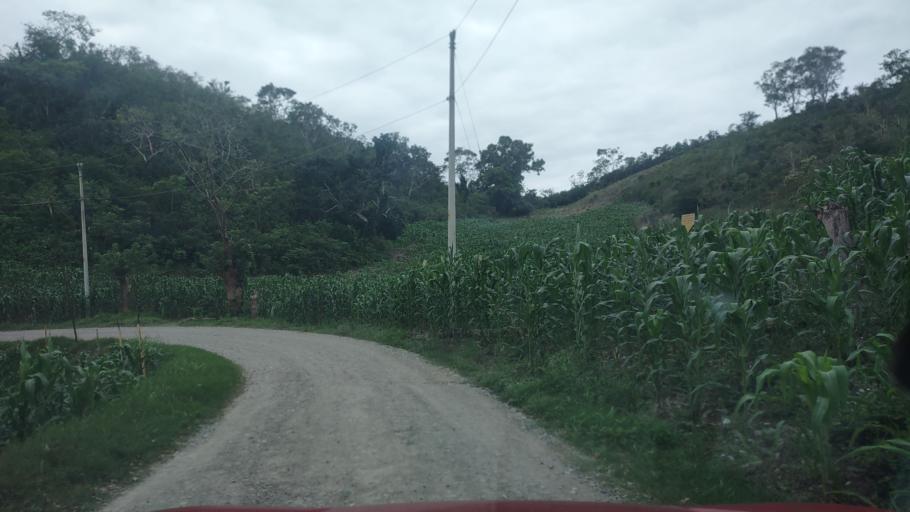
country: MX
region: Veracruz
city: Agua Dulce
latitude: 20.4201
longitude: -97.2688
